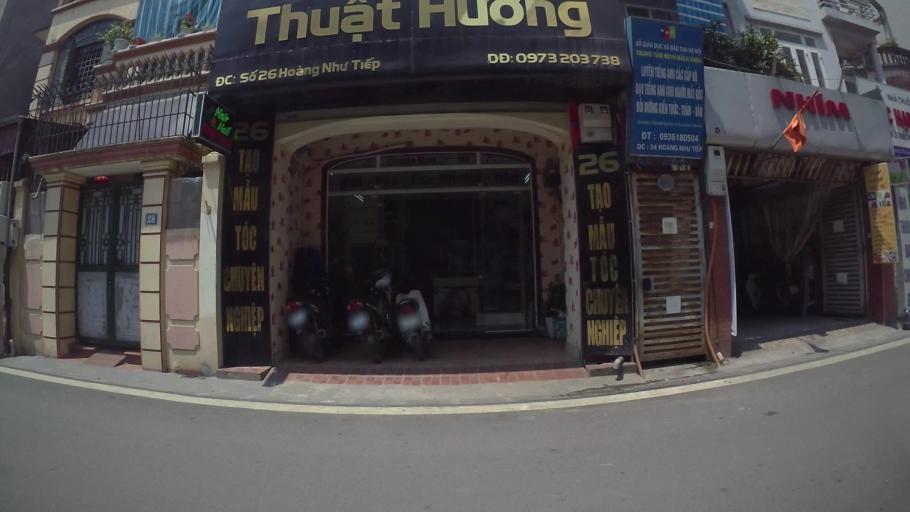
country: VN
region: Ha Noi
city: Hoan Kiem
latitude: 21.0445
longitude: 105.8752
